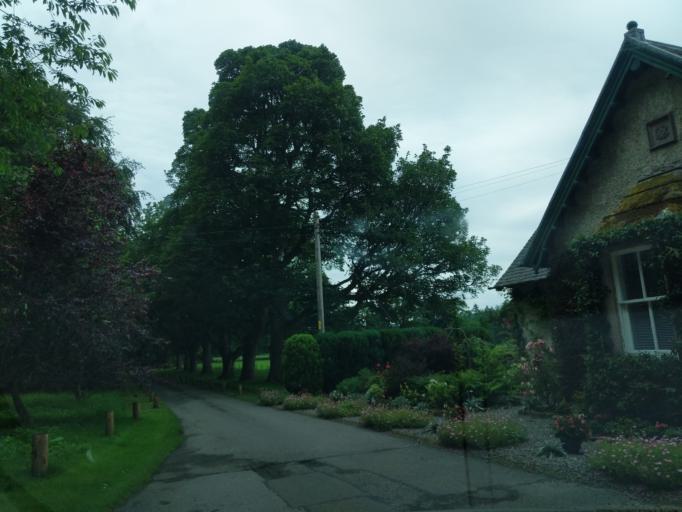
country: GB
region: Scotland
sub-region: Moray
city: Rothes
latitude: 57.4167
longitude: -3.3698
